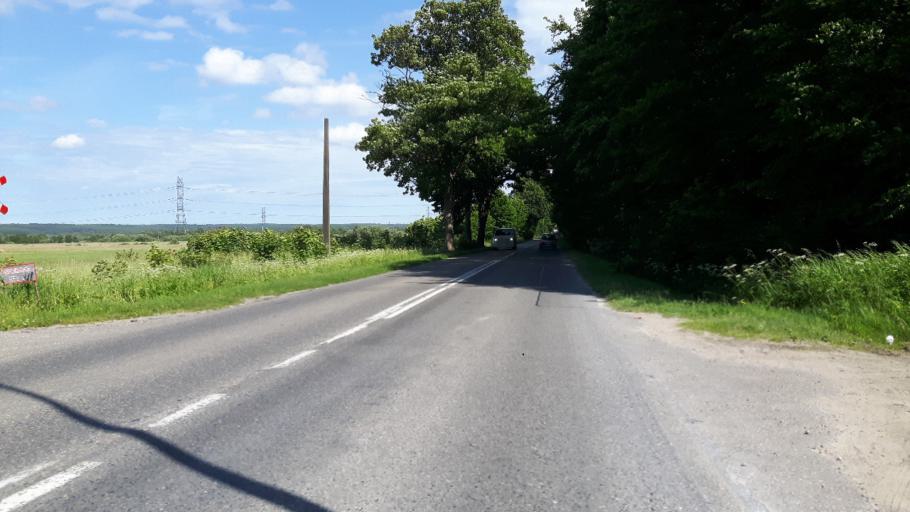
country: PL
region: Pomeranian Voivodeship
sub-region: Powiat wejherowski
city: Orle
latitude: 54.6462
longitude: 18.1148
